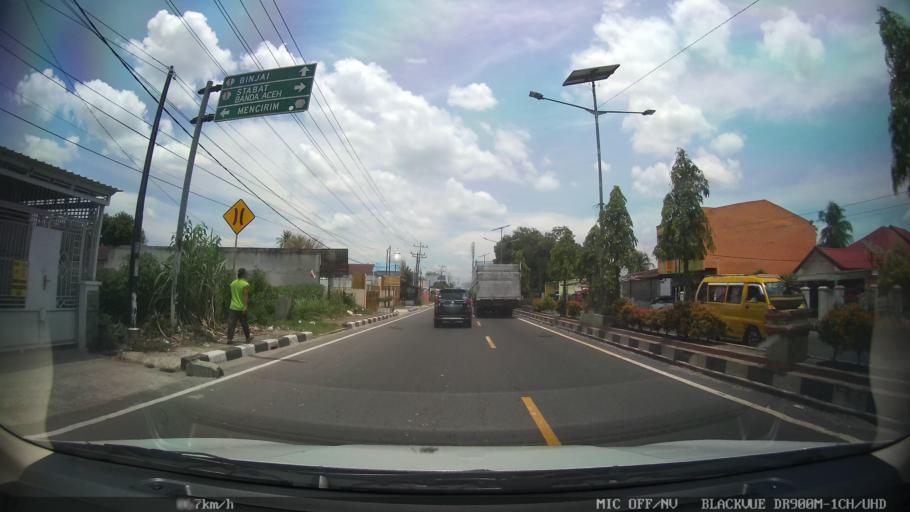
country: ID
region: North Sumatra
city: Binjai
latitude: 3.6073
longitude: 98.5222
